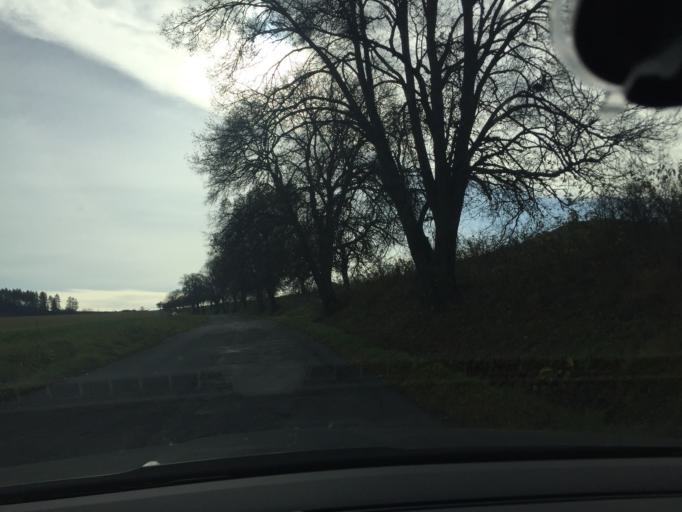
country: SK
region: Presovsky
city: Spisske Podhradie
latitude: 49.0045
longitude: 20.7766
